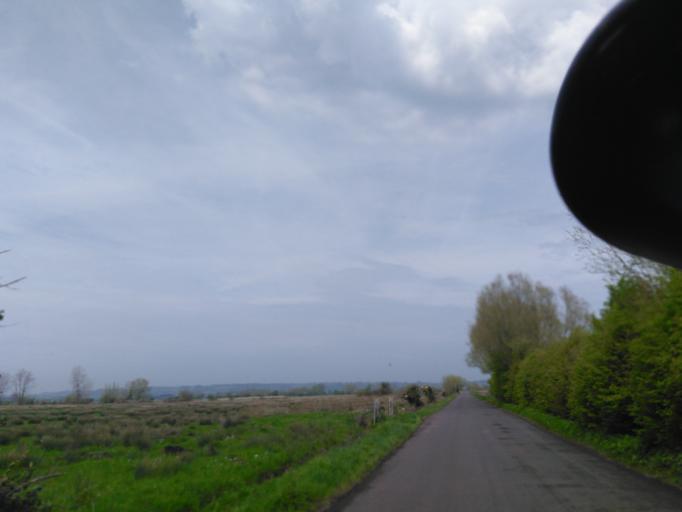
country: GB
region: England
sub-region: Somerset
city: Langport
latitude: 51.0922
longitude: -2.8205
